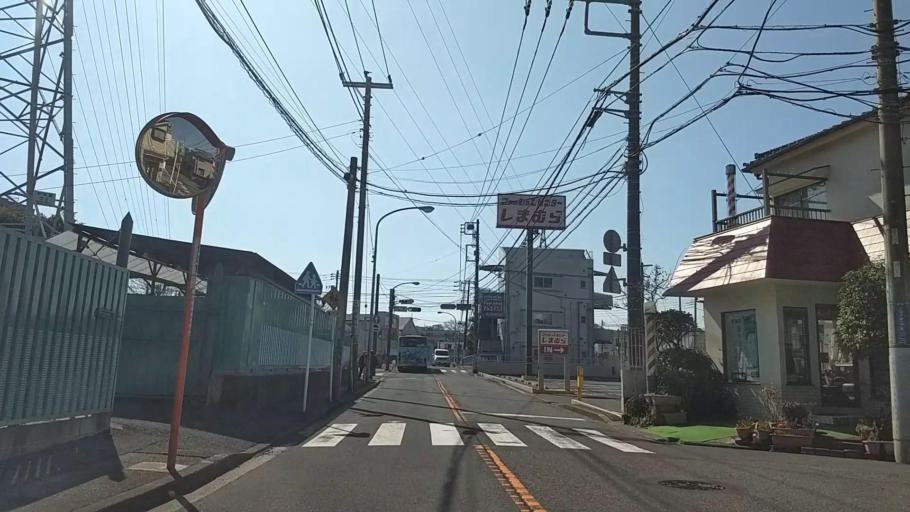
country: JP
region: Kanagawa
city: Kamakura
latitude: 35.3633
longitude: 139.5407
